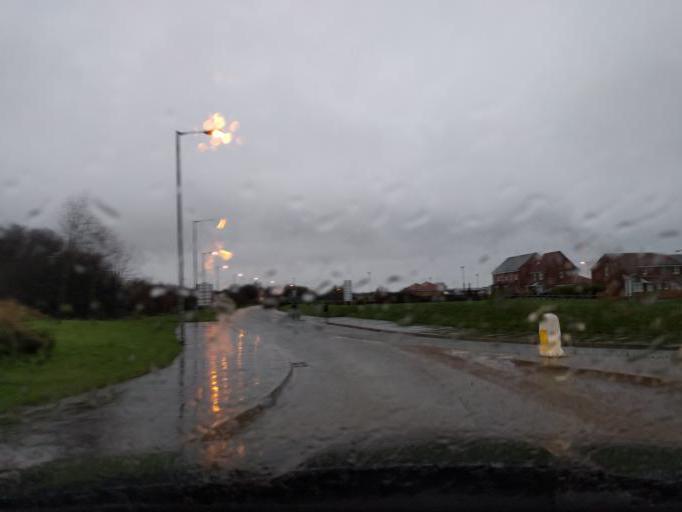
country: GB
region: England
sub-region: Northumberland
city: Lynemouth
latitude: 55.1815
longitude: -1.5495
